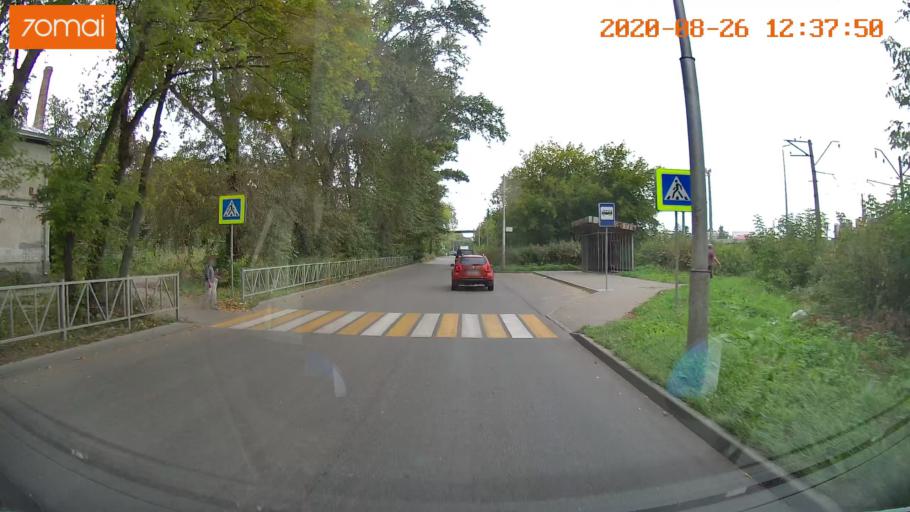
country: RU
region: Rjazan
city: Ryazan'
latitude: 54.6064
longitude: 39.7656
